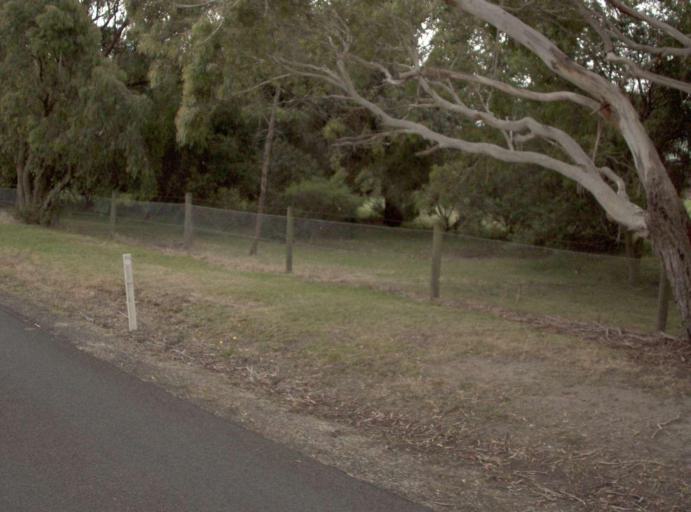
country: AU
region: Victoria
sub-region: Bass Coast
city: Cowes
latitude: -38.4236
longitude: 145.4408
